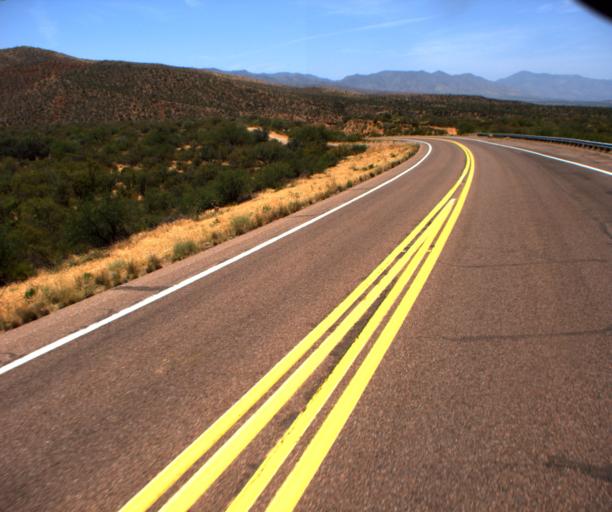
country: US
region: Arizona
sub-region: Gila County
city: Tonto Basin
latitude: 33.7249
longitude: -111.2062
